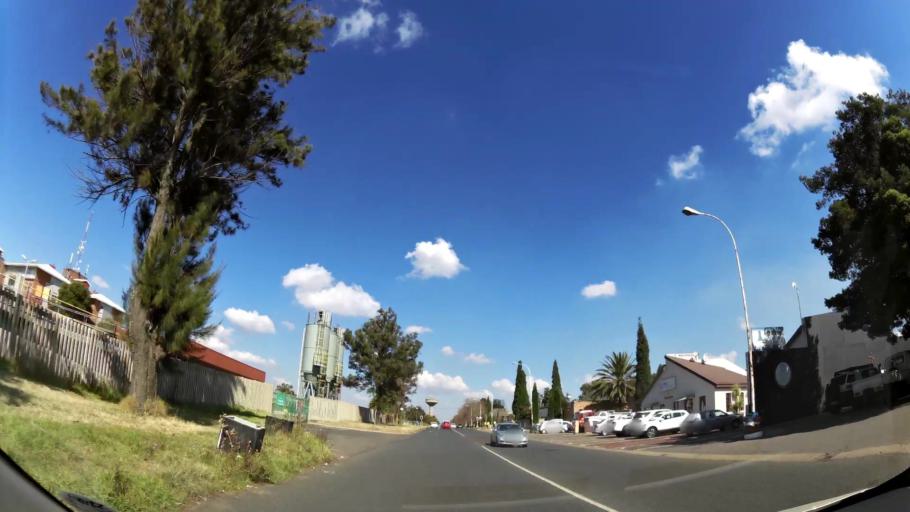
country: ZA
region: Mpumalanga
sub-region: Nkangala District Municipality
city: Witbank
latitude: -25.8830
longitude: 29.2304
